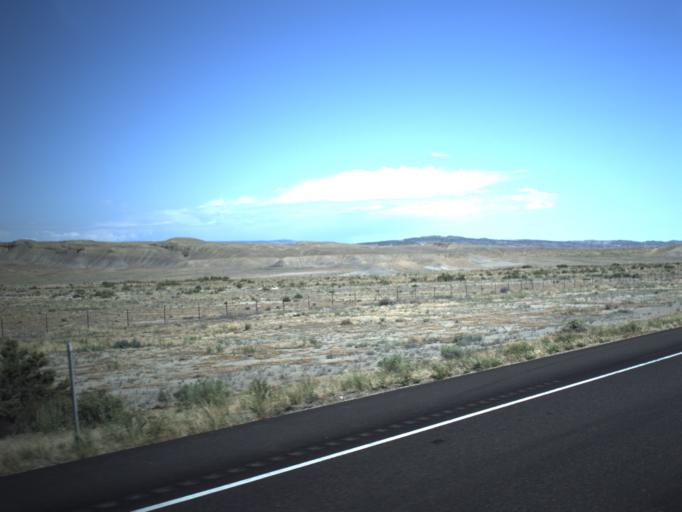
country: US
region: Utah
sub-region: Carbon County
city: East Carbon City
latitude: 39.0759
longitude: -110.3167
